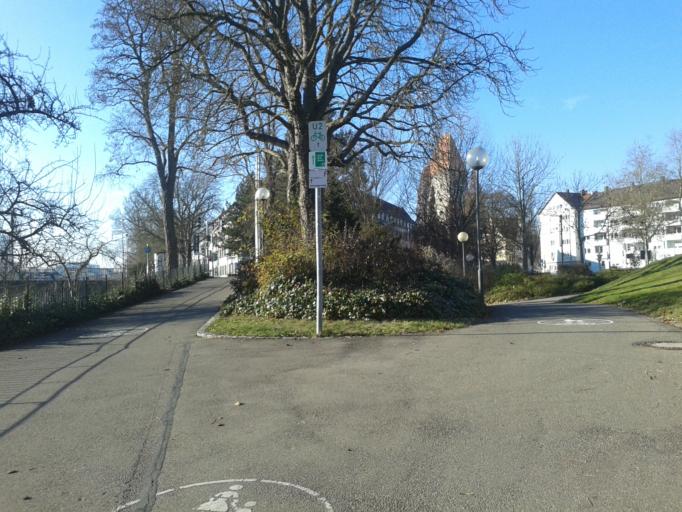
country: DE
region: Bavaria
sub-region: Swabia
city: Neu-Ulm
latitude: 48.3995
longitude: 10.0040
